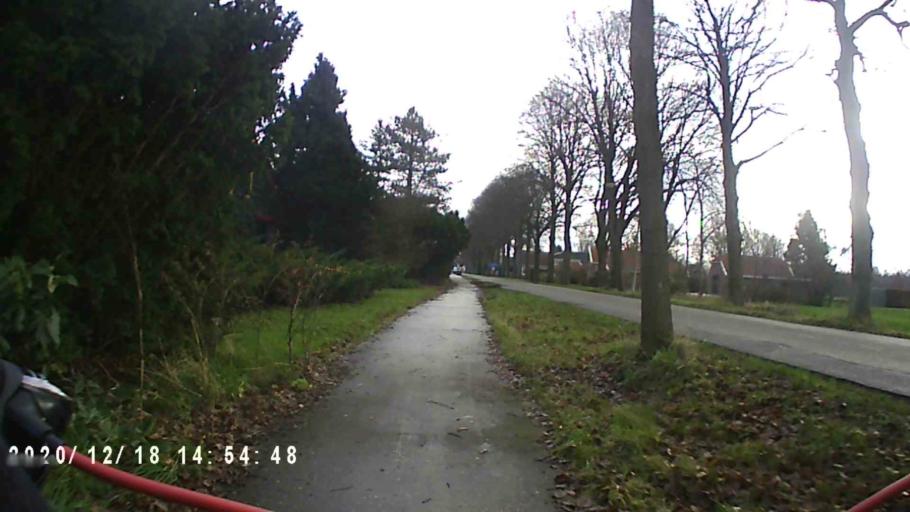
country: NL
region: Groningen
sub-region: Gemeente Haren
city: Haren
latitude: 53.1875
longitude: 6.6829
